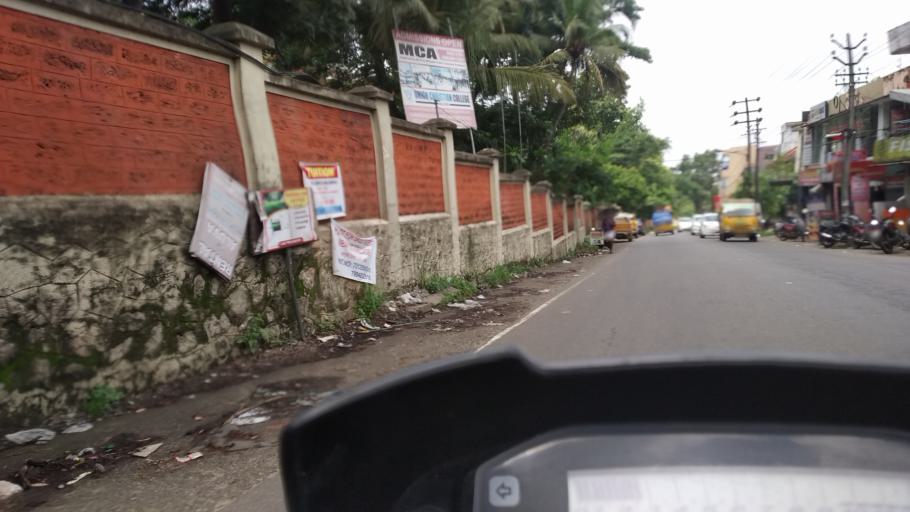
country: IN
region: Kerala
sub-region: Ernakulam
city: Aluva
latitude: 10.1250
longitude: 76.3339
